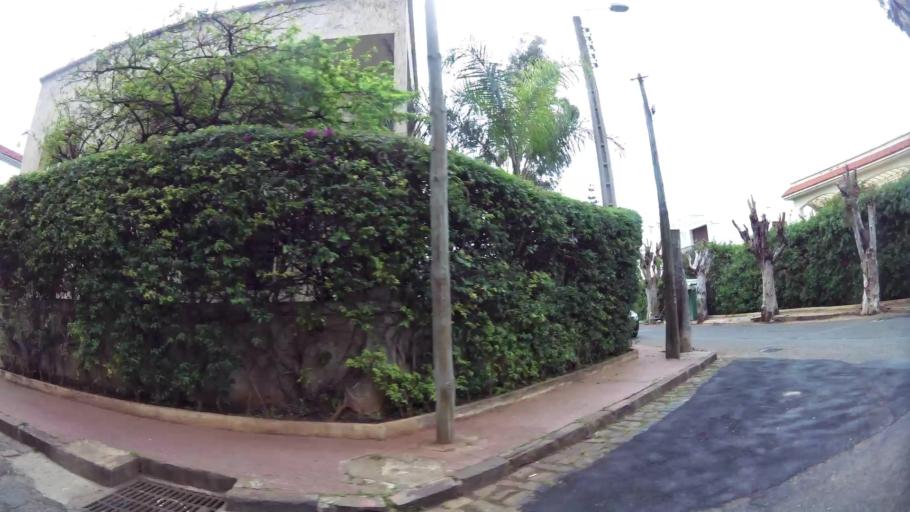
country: MA
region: Grand Casablanca
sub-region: Casablanca
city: Casablanca
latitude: 33.5619
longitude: -7.6348
